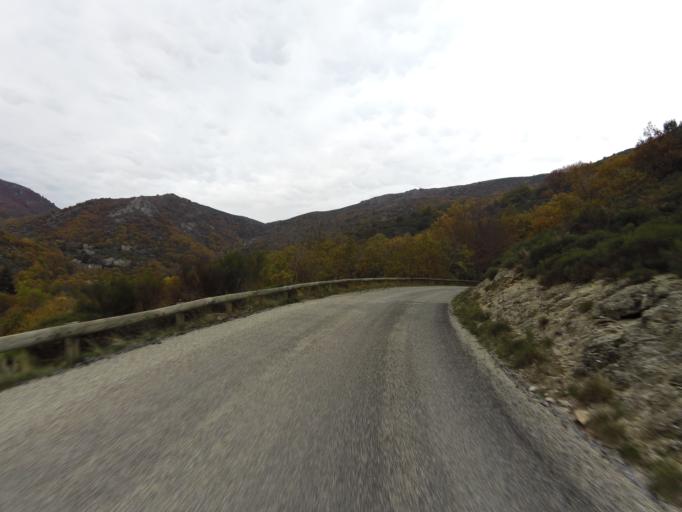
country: FR
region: Rhone-Alpes
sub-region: Departement de l'Ardeche
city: Les Vans
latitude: 44.5004
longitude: 4.0380
